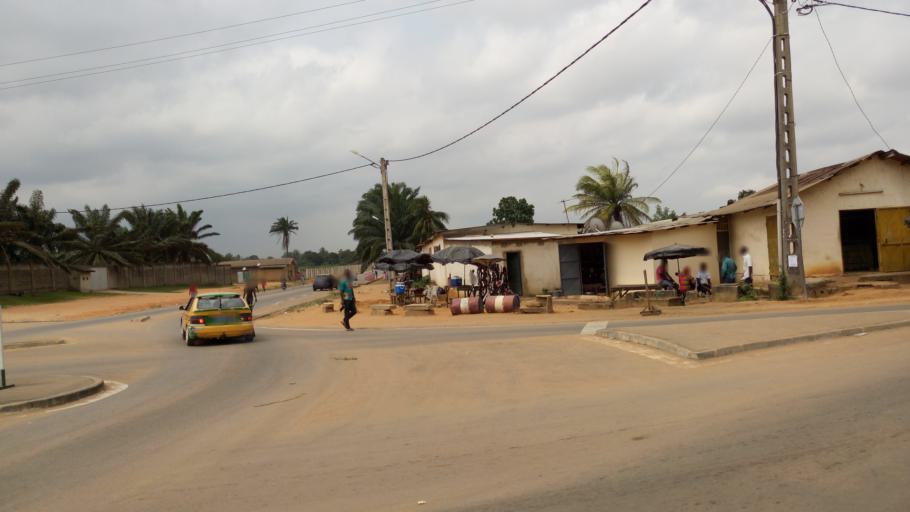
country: CI
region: Lagunes
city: Abobo
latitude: 5.4122
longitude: -4.0003
